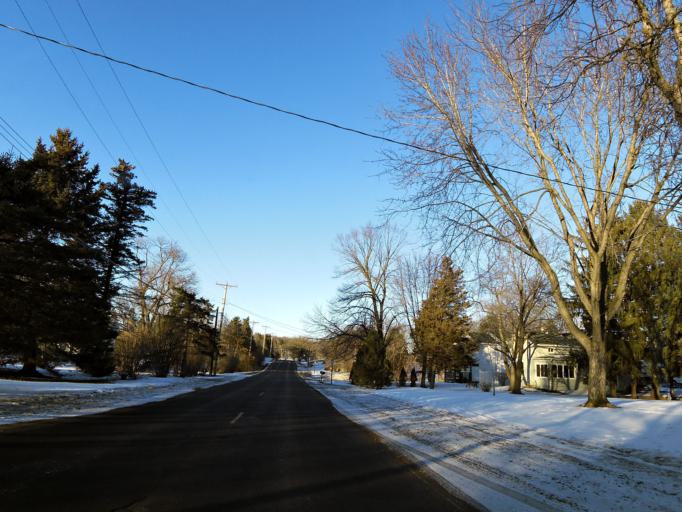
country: US
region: Minnesota
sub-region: Washington County
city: Cottage Grove
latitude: 44.8444
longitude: -92.8812
